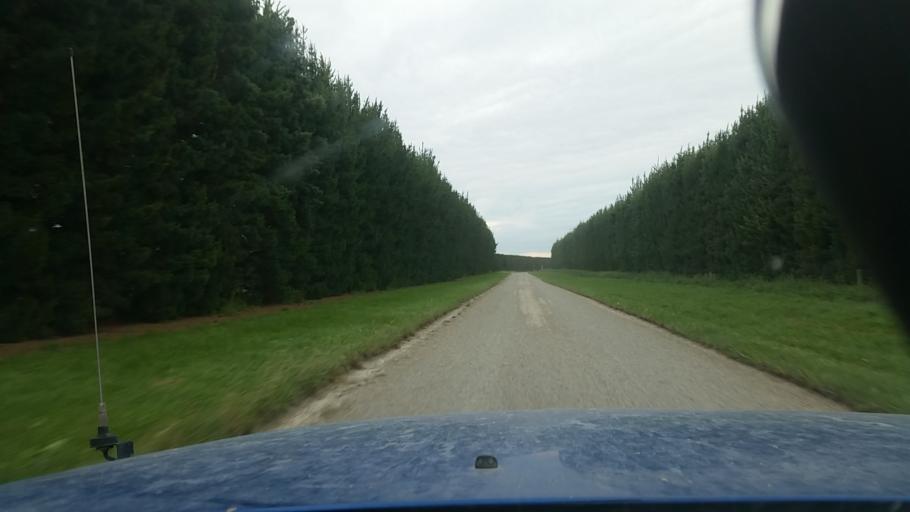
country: NZ
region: Canterbury
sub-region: Ashburton District
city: Tinwald
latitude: -43.9075
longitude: 171.5419
